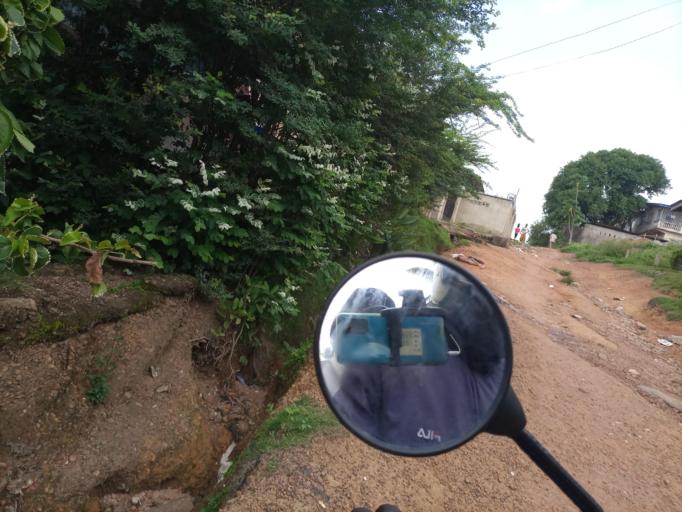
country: SL
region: Southern Province
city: Bo
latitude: 7.9527
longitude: -11.7342
